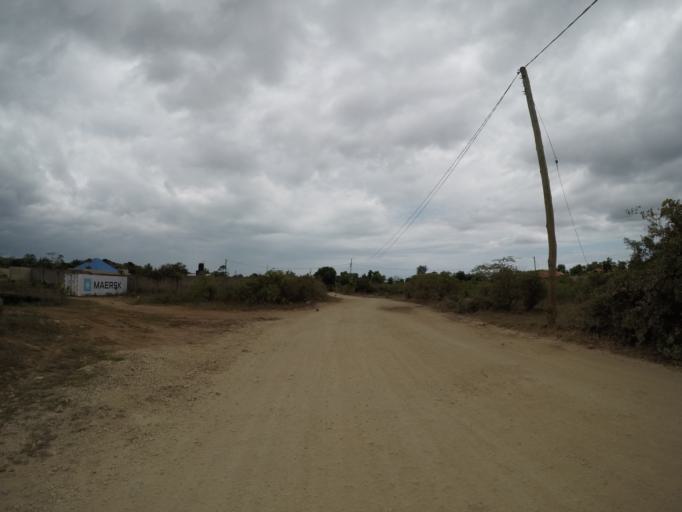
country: TZ
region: Zanzibar Central/South
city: Koani
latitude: -6.1956
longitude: 39.3096
